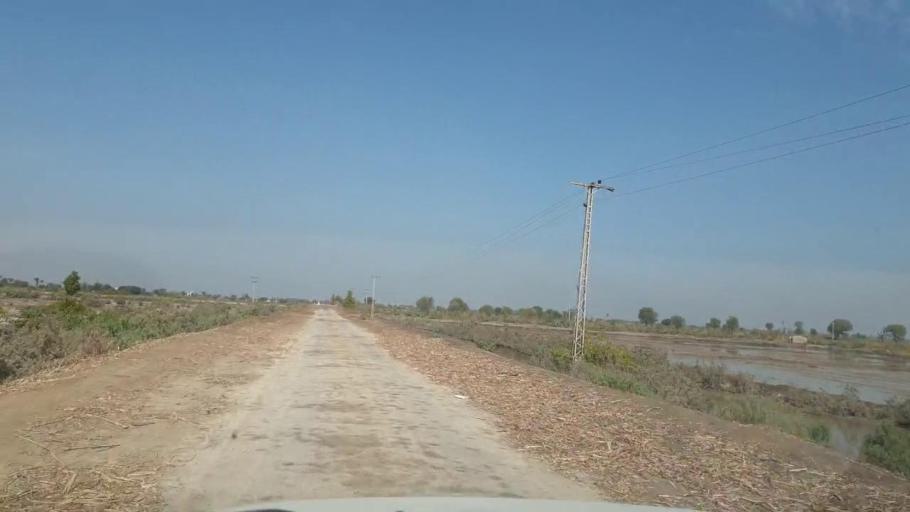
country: PK
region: Sindh
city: Pithoro
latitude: 25.5701
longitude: 69.2051
